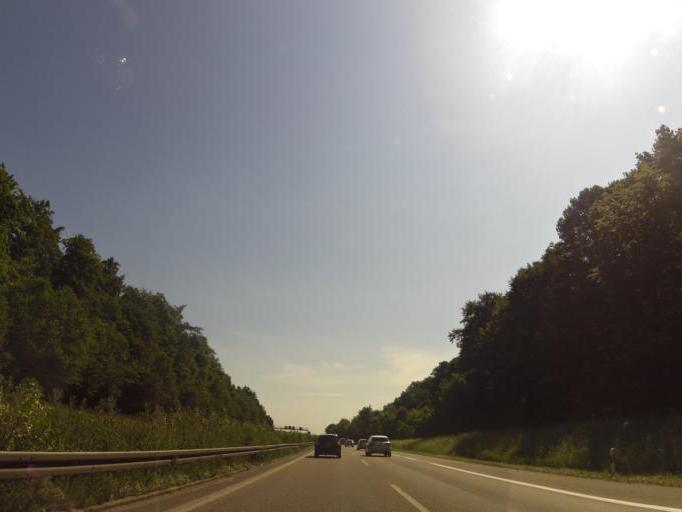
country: DE
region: Baden-Wuerttemberg
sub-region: Tuebingen Region
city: Bernstadt
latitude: 48.4545
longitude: 10.0666
